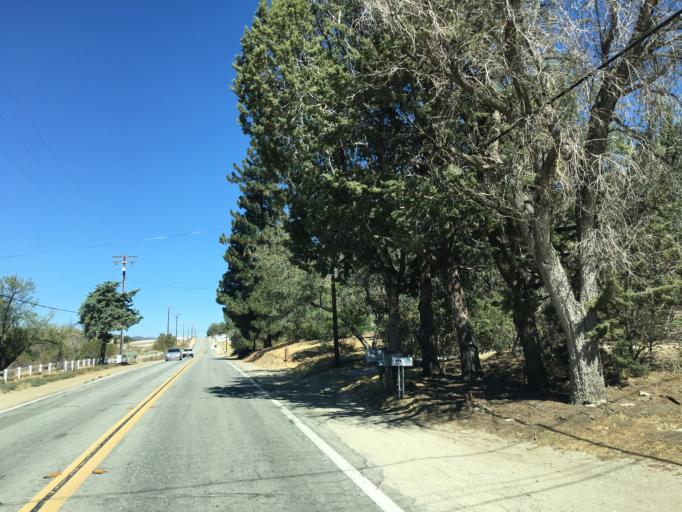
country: US
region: California
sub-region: Los Angeles County
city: Leona Valley
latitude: 34.6183
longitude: -118.2893
